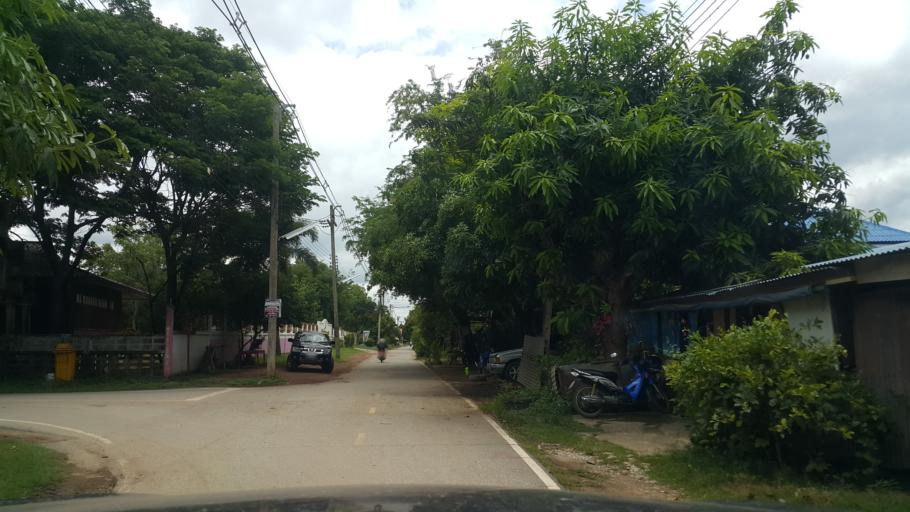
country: TH
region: Sukhothai
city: Kong Krailat
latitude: 16.9336
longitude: 99.9572
